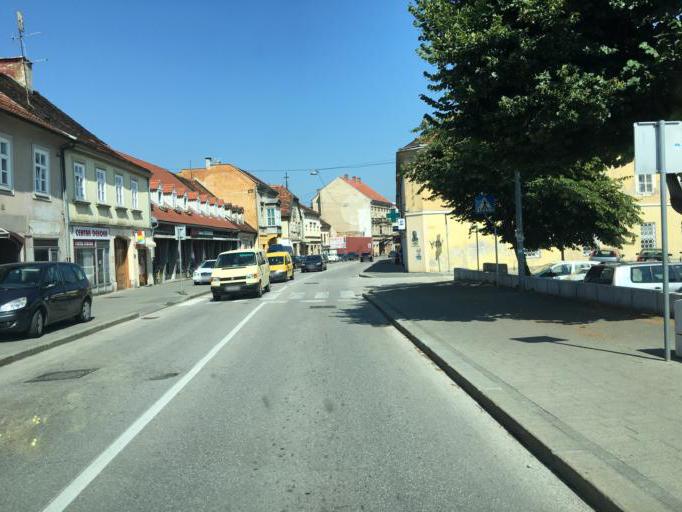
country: HR
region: Karlovacka
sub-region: Grad Karlovac
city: Karlovac
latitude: 45.4967
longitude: 15.5516
